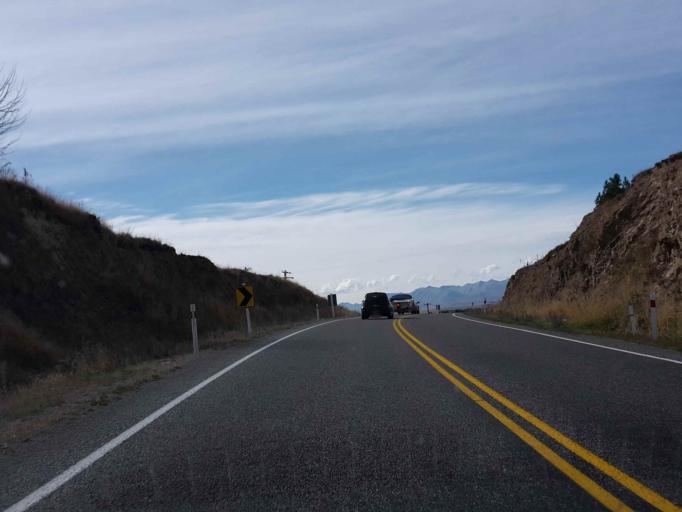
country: NZ
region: Canterbury
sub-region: Timaru District
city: Pleasant Point
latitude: -44.1958
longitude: 170.2826
